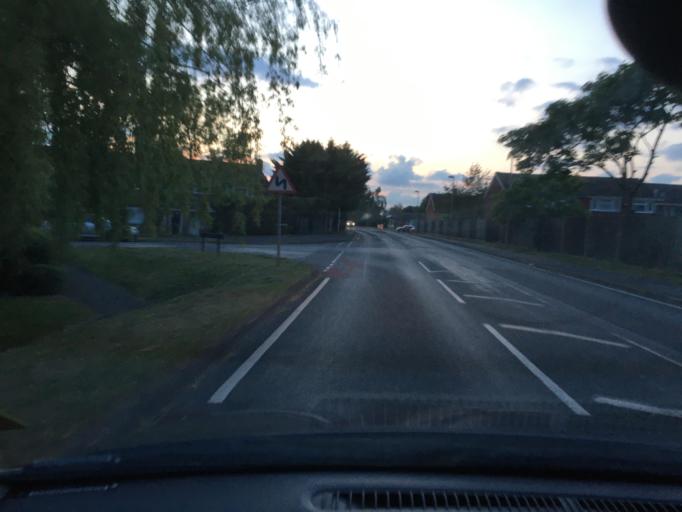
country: GB
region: England
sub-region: Bracknell Forest
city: Sandhurst
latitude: 51.3374
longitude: -0.7910
